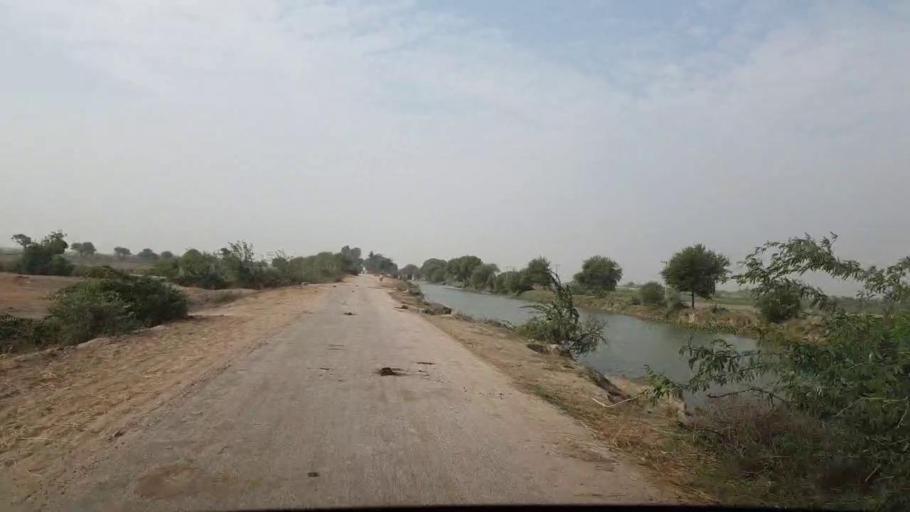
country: PK
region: Sindh
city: Chuhar Jamali
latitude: 24.3855
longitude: 67.9393
